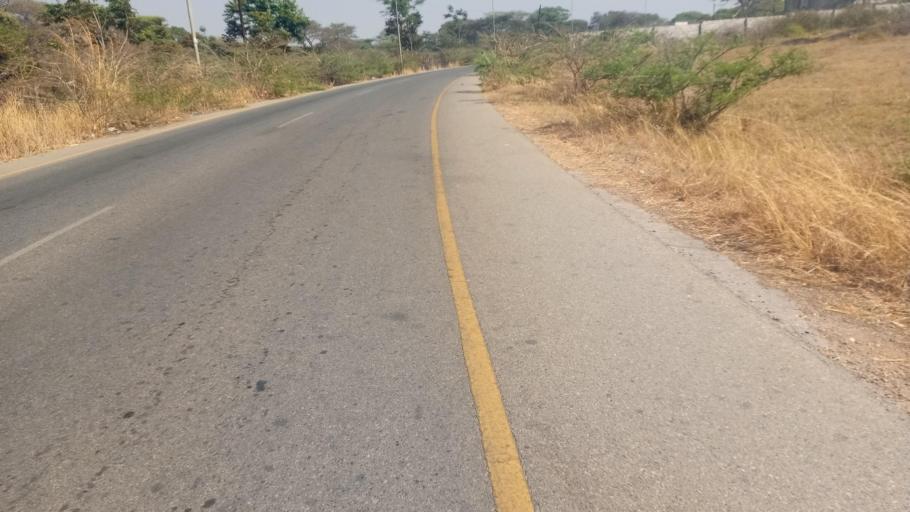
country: ZM
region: Lusaka
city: Lusaka
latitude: -15.4581
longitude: 28.4350
